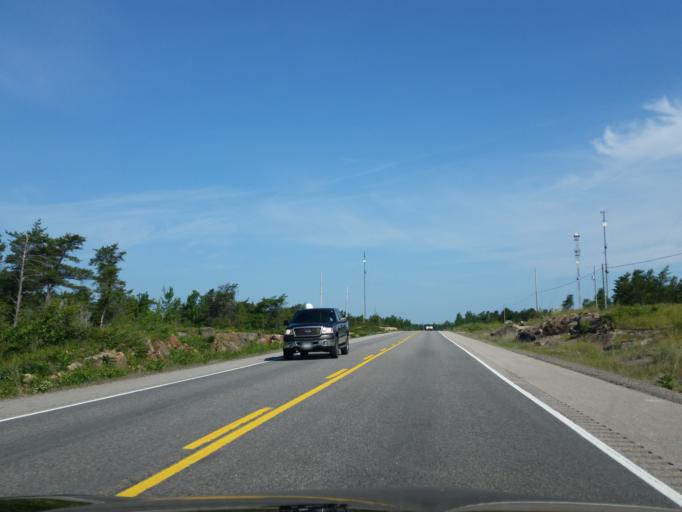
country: CA
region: Ontario
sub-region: Parry Sound District
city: Parry Sound
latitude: 45.7881
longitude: -80.5257
